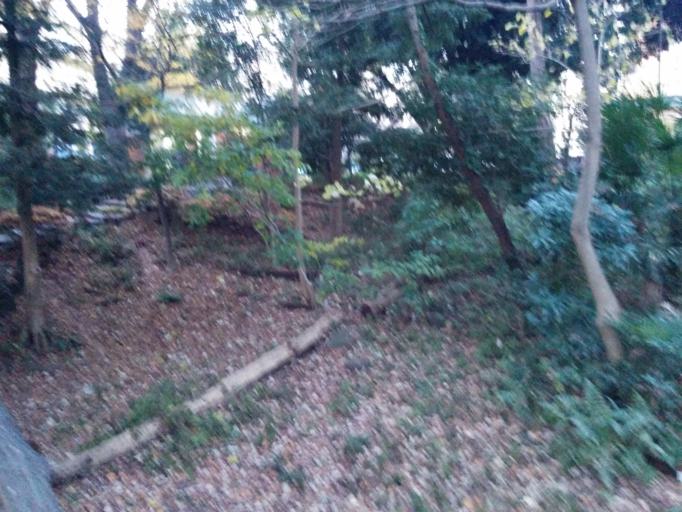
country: JP
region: Tokyo
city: Tokyo
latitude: 35.6531
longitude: 139.7261
